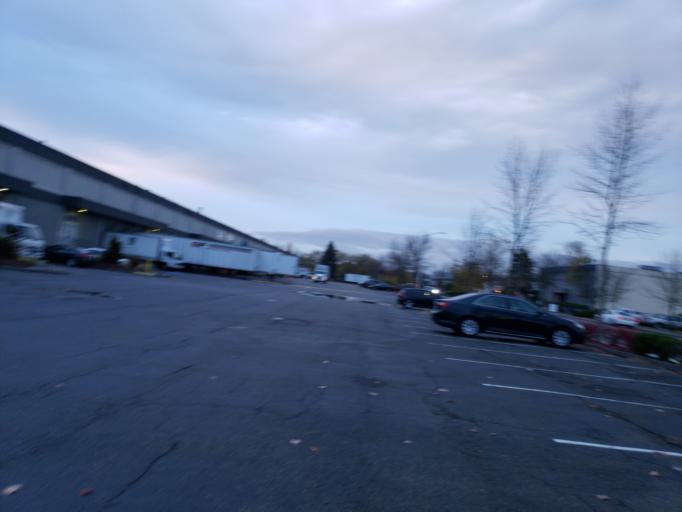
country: US
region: Washington
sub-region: King County
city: Tukwila
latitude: 47.4431
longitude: -122.2548
